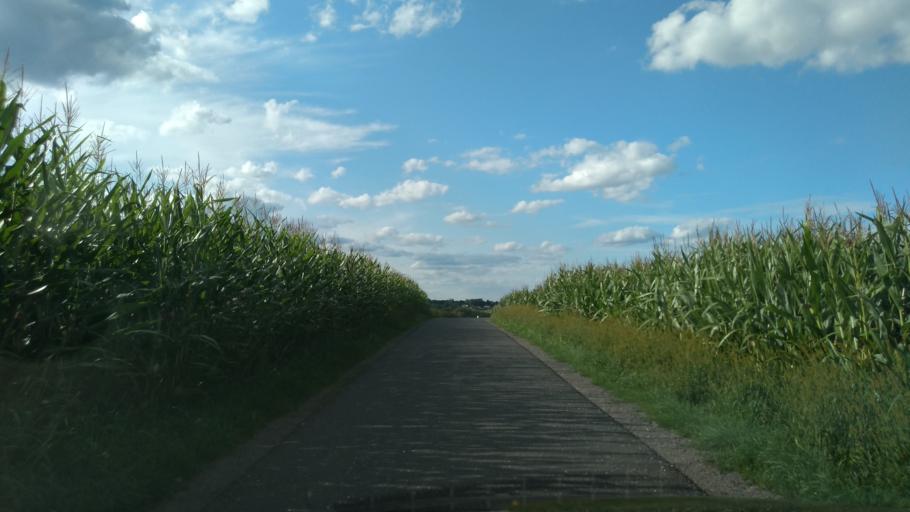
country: DE
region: North Rhine-Westphalia
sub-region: Regierungsbezirk Koln
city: Much
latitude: 50.8633
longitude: 7.3791
